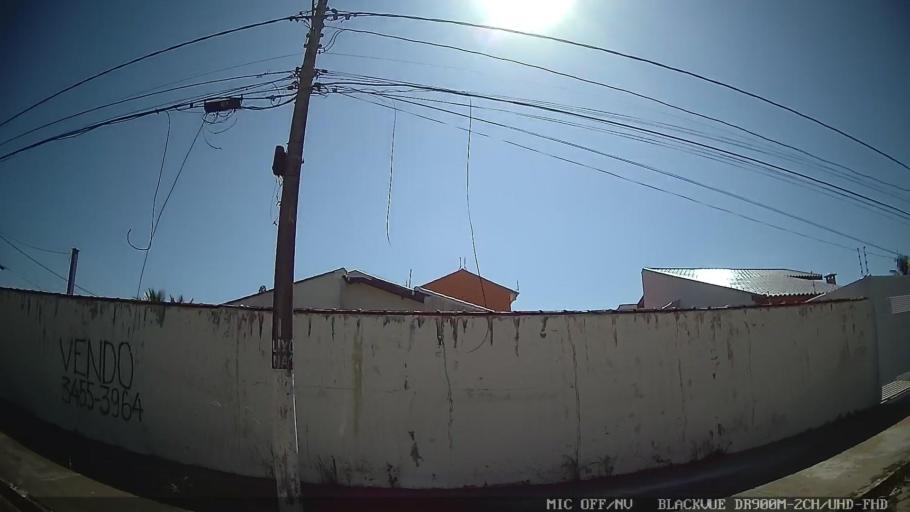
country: BR
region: Sao Paulo
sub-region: Peruibe
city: Peruibe
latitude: -24.2888
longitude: -46.9551
